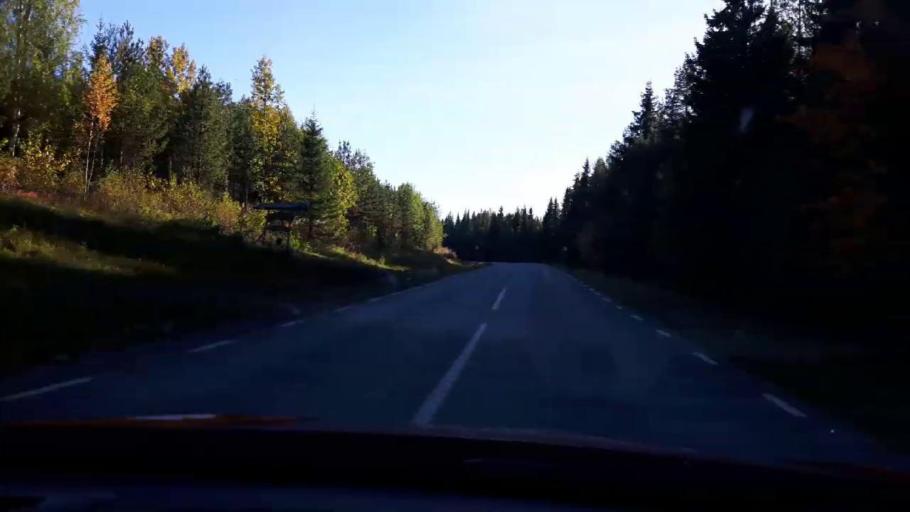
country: SE
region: Jaemtland
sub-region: OEstersunds Kommun
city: Lit
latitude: 63.7964
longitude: 14.7075
